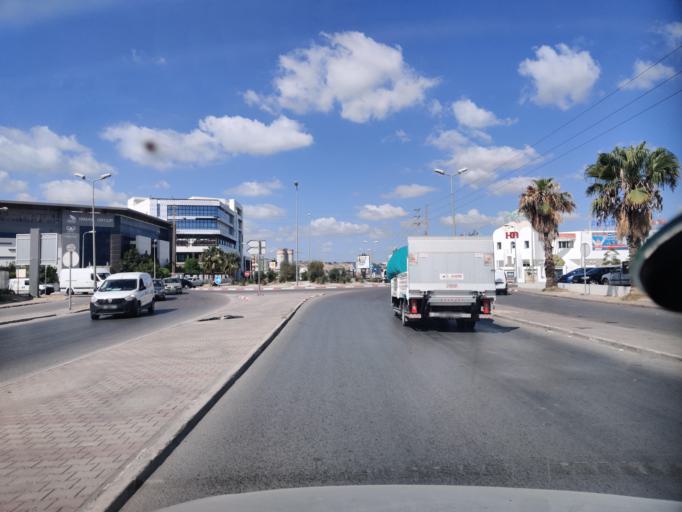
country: TN
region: Bin 'Arus
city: Ben Arous
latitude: 36.7753
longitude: 10.2155
